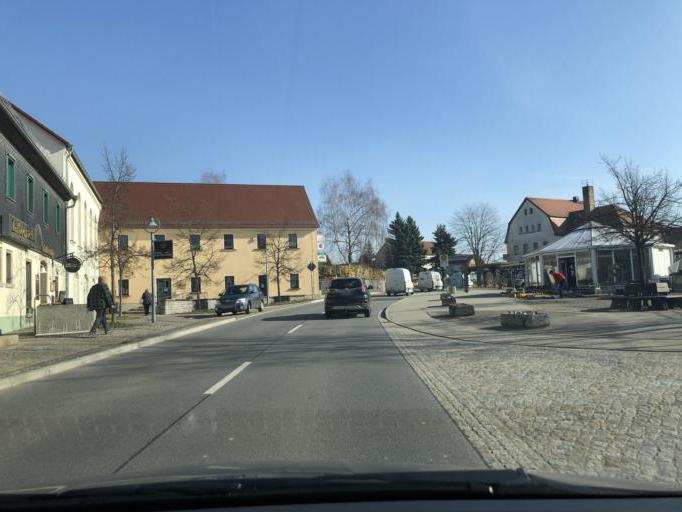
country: DE
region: Saxony
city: Rammenau
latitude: 51.1539
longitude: 14.1353
